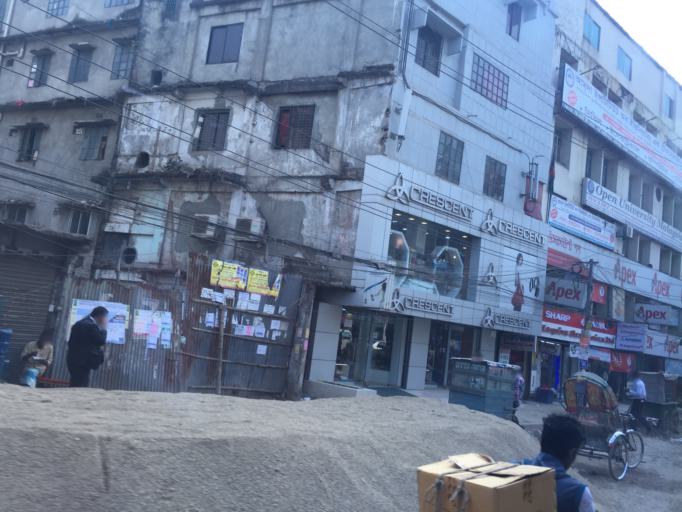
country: BD
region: Dhaka
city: Paltan
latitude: 23.7582
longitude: 90.4177
